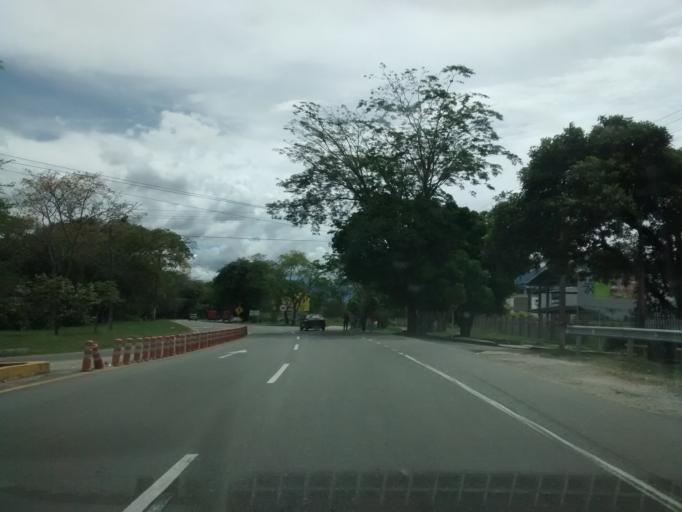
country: CO
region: Tolima
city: Ibague
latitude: 4.4010
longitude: -75.1477
